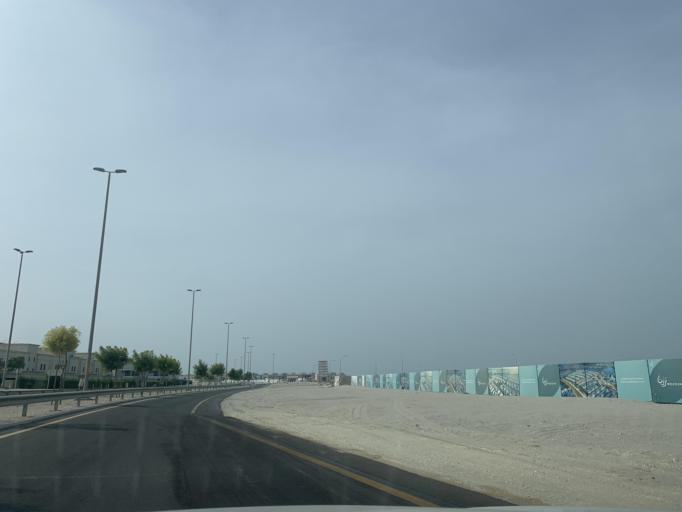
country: BH
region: Muharraq
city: Al Muharraq
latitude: 26.3152
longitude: 50.6323
